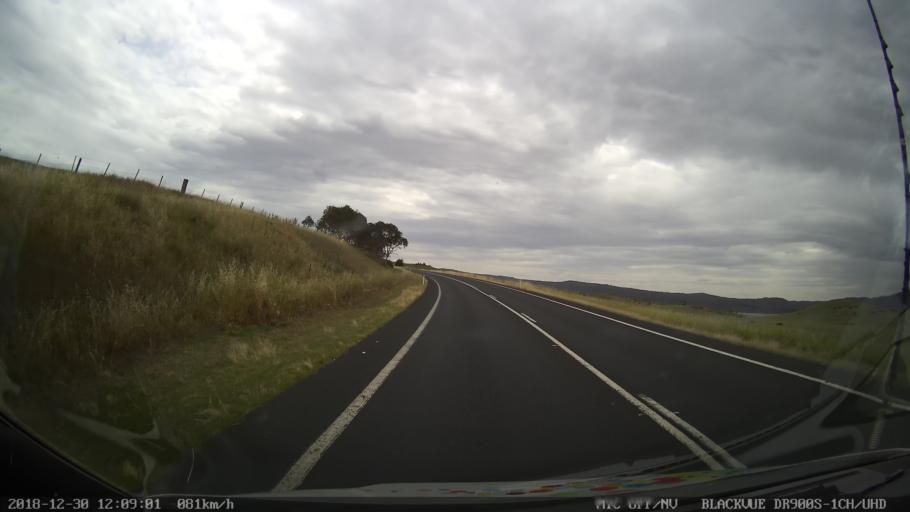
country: AU
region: New South Wales
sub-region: Snowy River
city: Jindabyne
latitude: -36.3895
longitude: 148.5978
